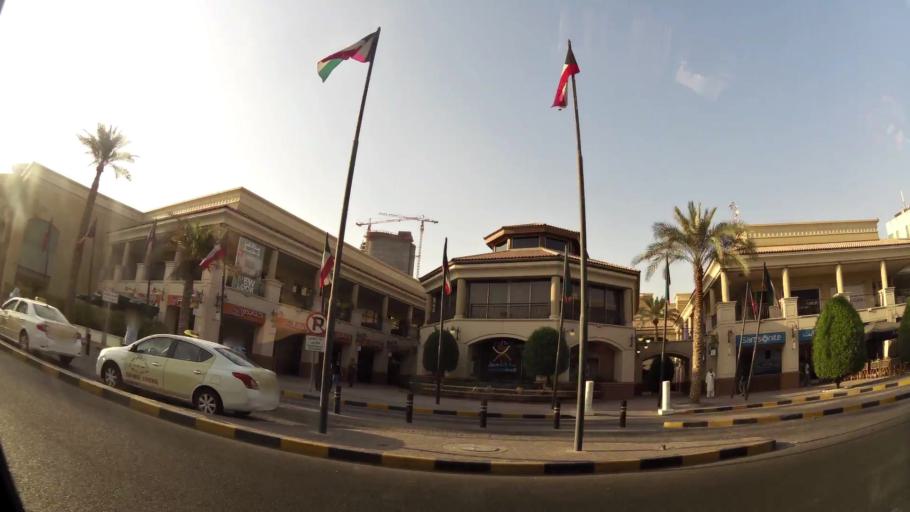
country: KW
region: Muhafazat Hawalli
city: As Salimiyah
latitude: 29.3378
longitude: 48.0662
